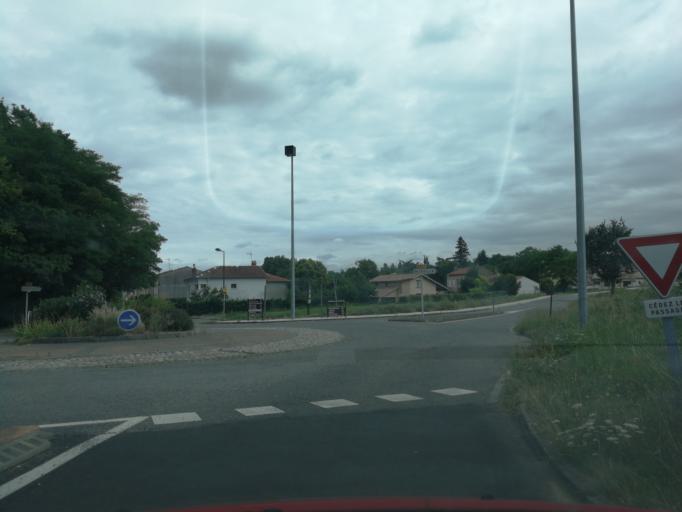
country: FR
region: Midi-Pyrenees
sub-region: Departement de la Haute-Garonne
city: Auzeville-Tolosane
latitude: 43.5319
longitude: 1.4770
